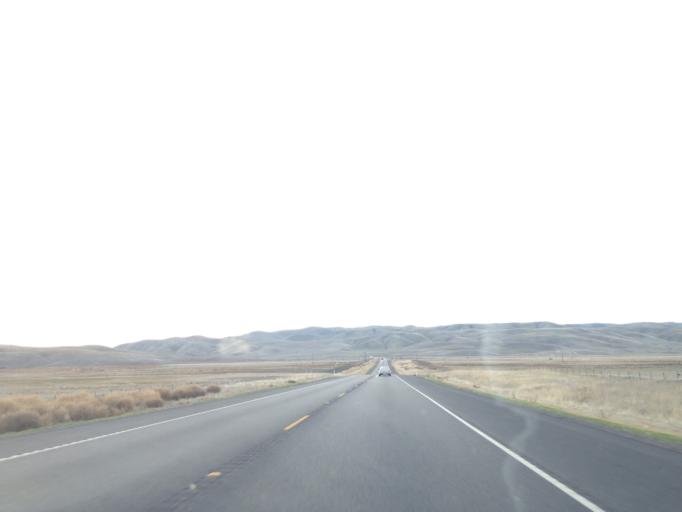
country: US
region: California
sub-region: San Luis Obispo County
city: Shandon
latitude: 35.7365
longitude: -120.2733
